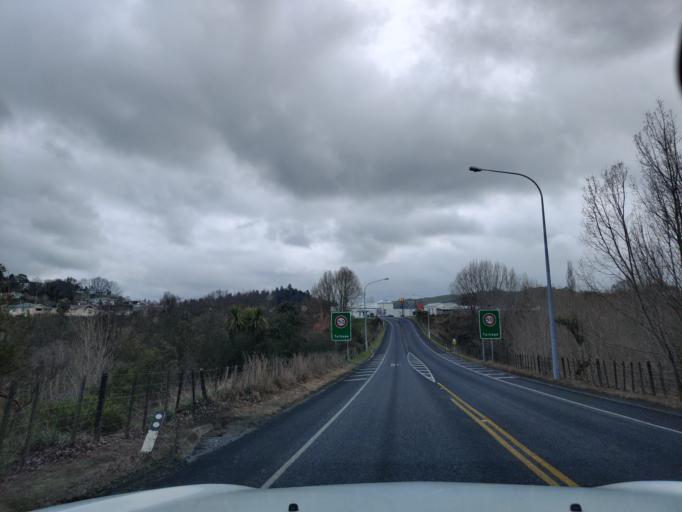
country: NZ
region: Manawatu-Wanganui
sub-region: Ruapehu District
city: Waiouru
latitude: -39.6820
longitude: 175.8007
